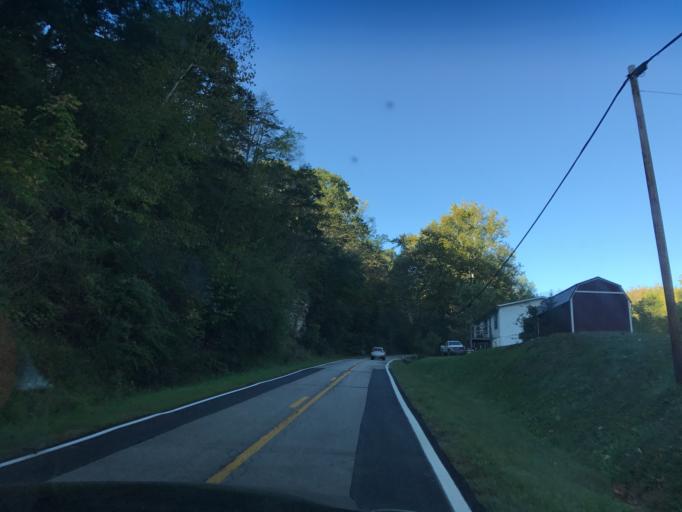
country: US
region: West Virginia
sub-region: Ritchie County
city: Harrisville
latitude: 39.3021
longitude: -81.1233
